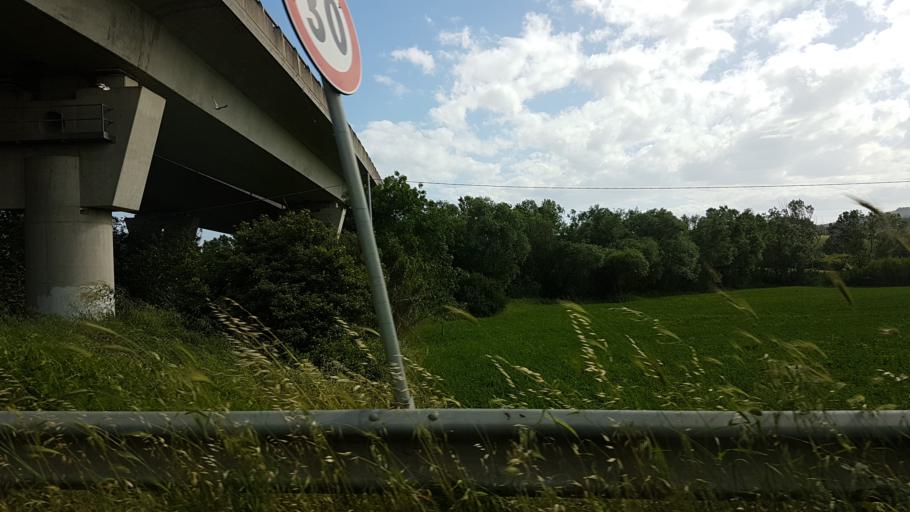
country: IT
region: Tuscany
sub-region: Provincia di Livorno
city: Rosignano Marittimo
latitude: 43.4380
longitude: 10.4867
